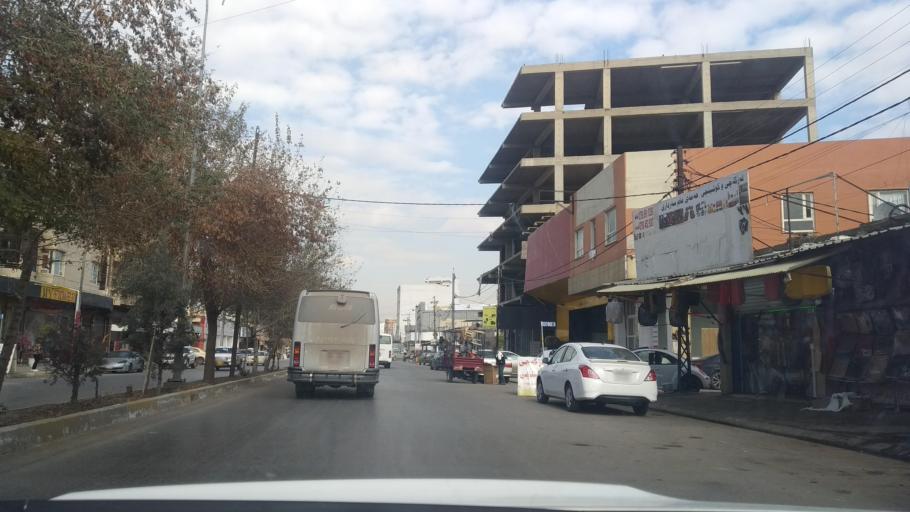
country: IQ
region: Arbil
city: Erbil
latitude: 36.1748
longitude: 44.0367
